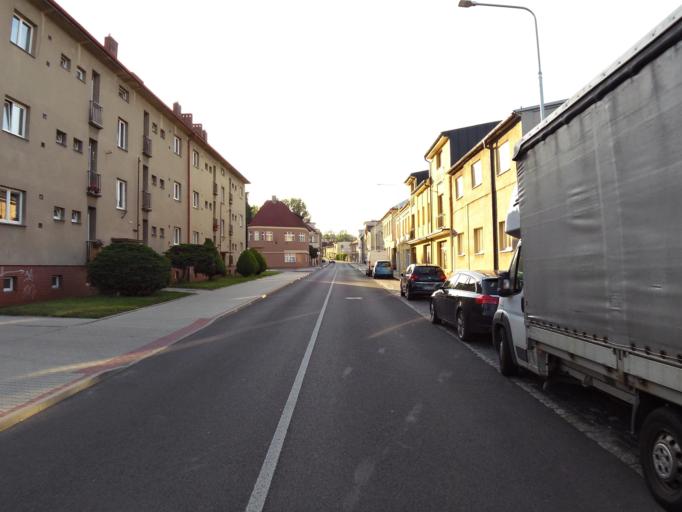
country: CZ
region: Central Bohemia
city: Mnichovo Hradiste
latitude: 50.5198
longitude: 14.9756
